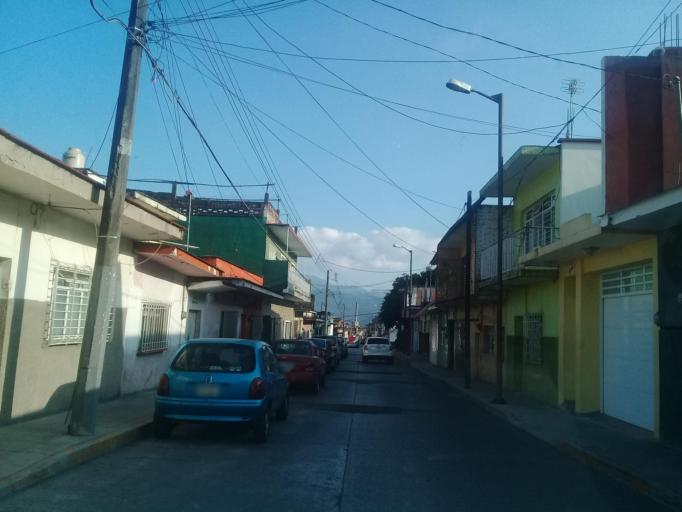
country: MX
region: Veracruz
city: Orizaba
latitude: 18.8560
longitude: -97.1091
